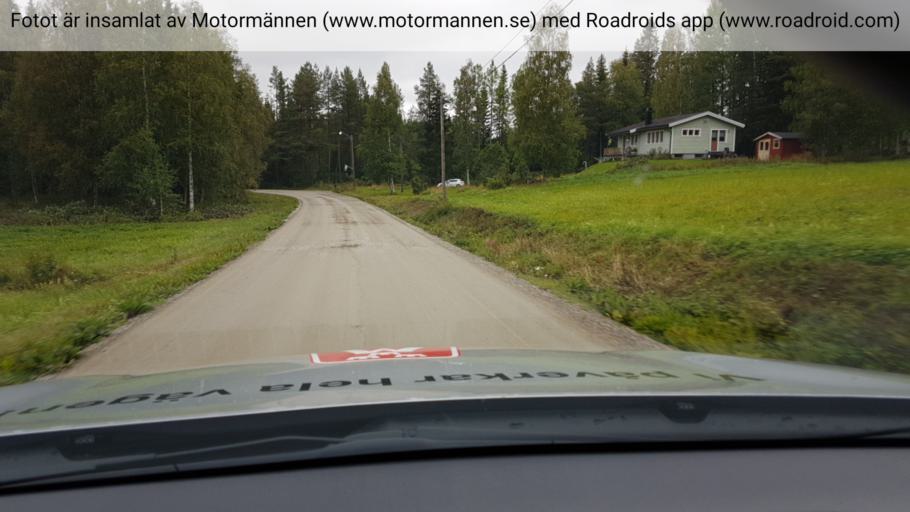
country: SE
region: Jaemtland
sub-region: Braecke Kommun
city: Braecke
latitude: 62.7768
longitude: 15.4786
